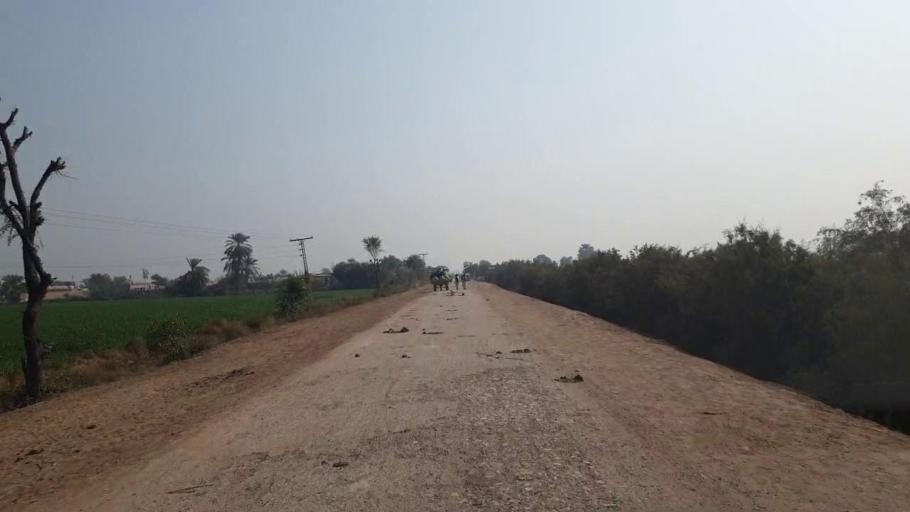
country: PK
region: Sindh
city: Hala
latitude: 25.9388
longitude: 68.4536
